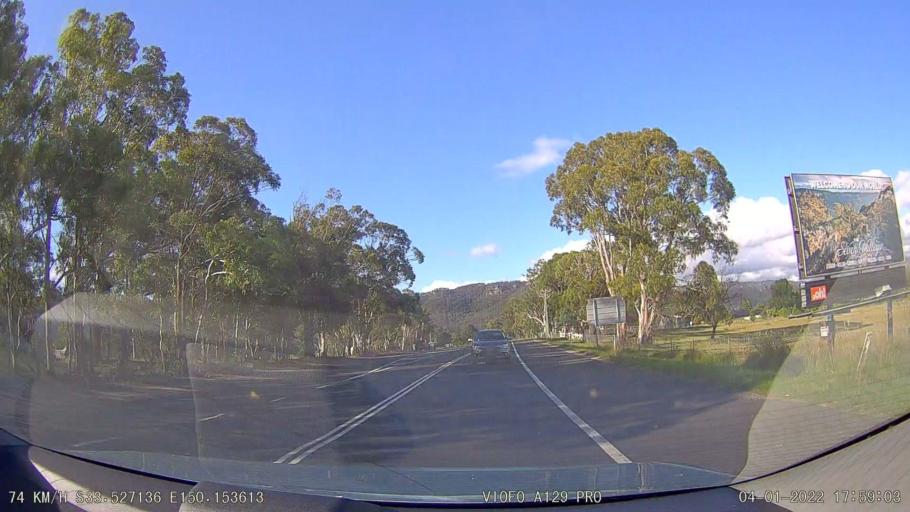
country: AU
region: New South Wales
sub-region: Lithgow
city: Bowenfels
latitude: -33.5273
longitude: 150.1535
